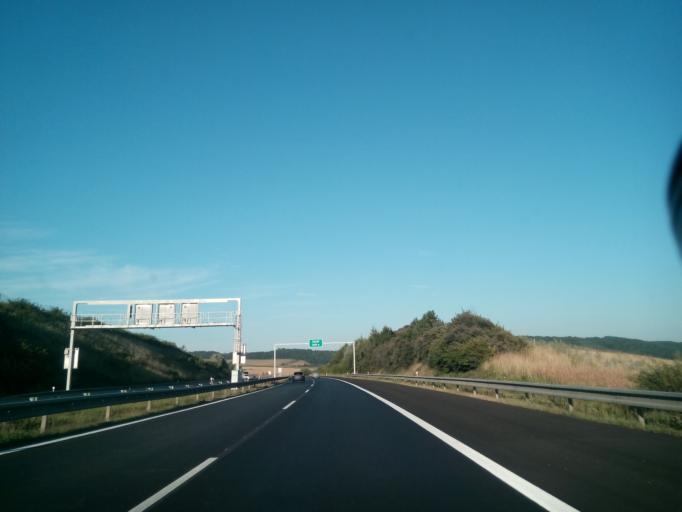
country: SK
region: Kosicky
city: Krompachy
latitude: 48.9959
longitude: 20.9160
